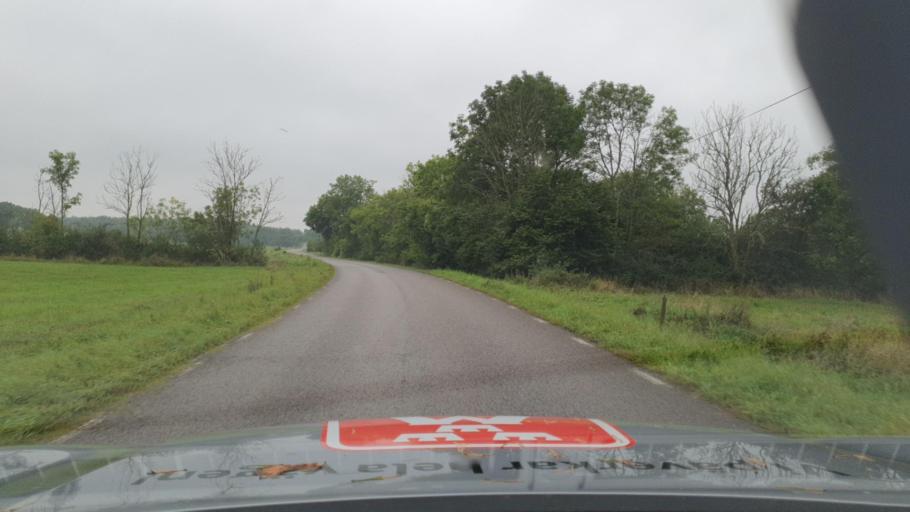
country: SE
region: Gotland
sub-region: Gotland
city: Visby
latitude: 57.7773
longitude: 18.4983
